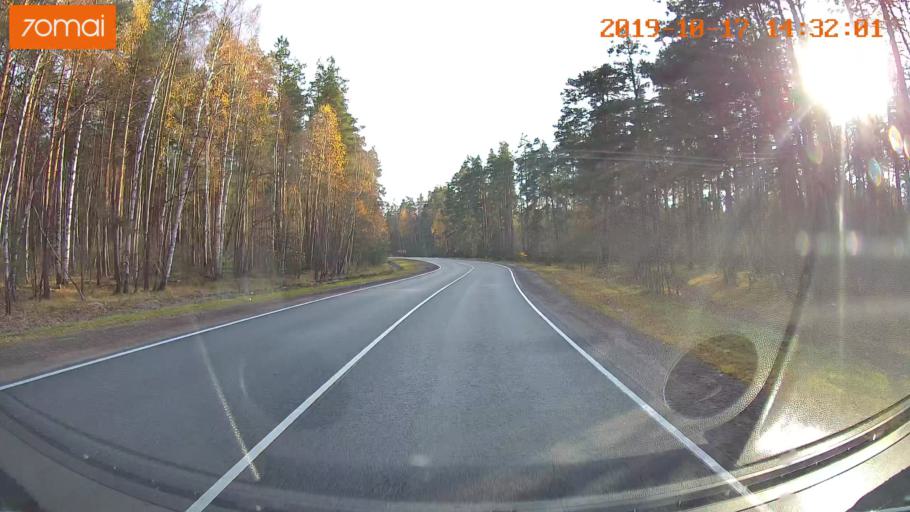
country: RU
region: Rjazan
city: Solotcha
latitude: 54.9317
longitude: 39.9741
